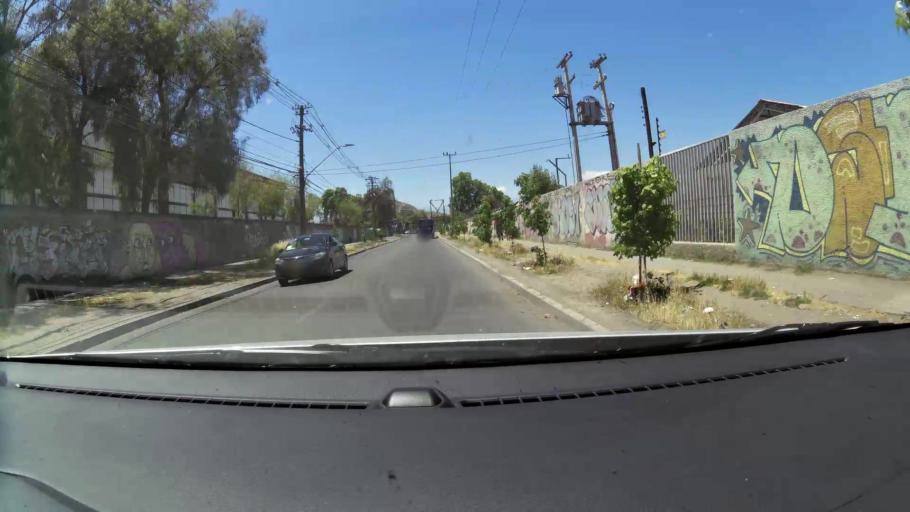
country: CL
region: Santiago Metropolitan
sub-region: Provincia de Maipo
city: San Bernardo
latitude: -33.6180
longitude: -70.7007
